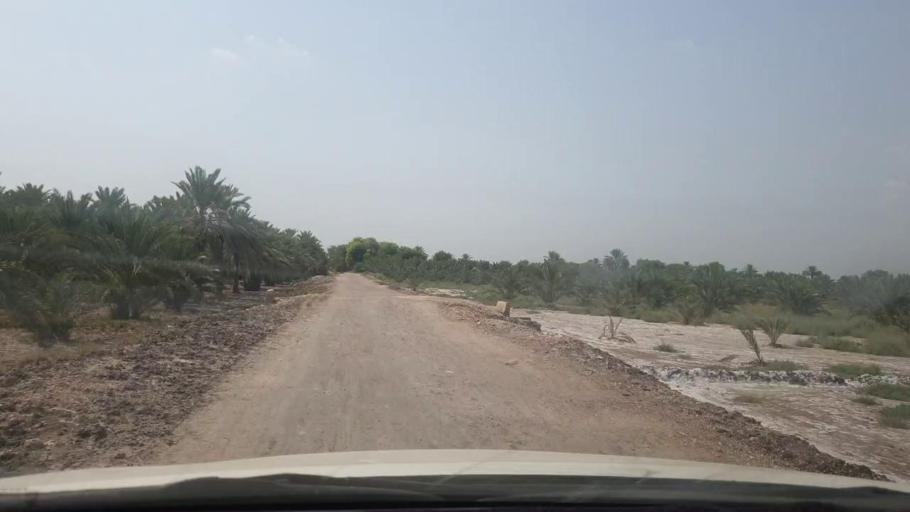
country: PK
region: Sindh
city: Khairpur
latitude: 27.5606
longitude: 68.8490
